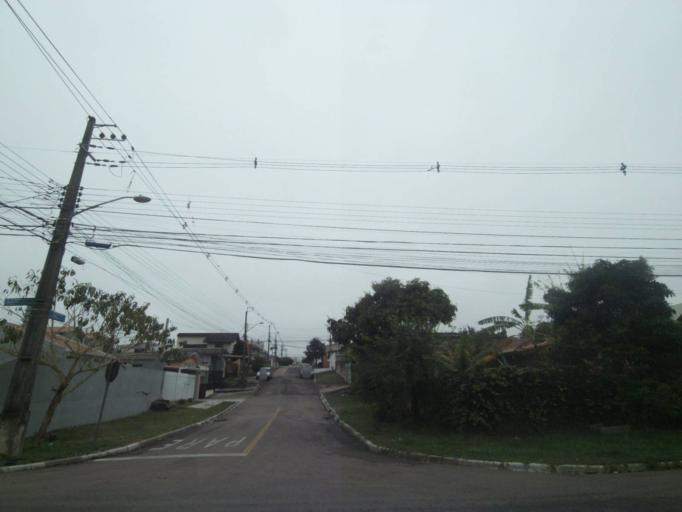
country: BR
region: Parana
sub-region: Curitiba
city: Curitiba
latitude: -25.5042
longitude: -49.3019
